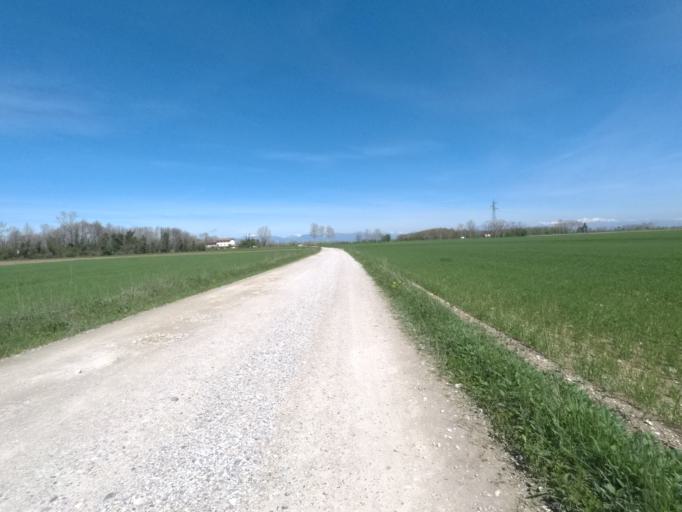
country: IT
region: Friuli Venezia Giulia
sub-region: Provincia di Udine
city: Camino al Tagliamento
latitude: 45.9631
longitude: 12.9166
